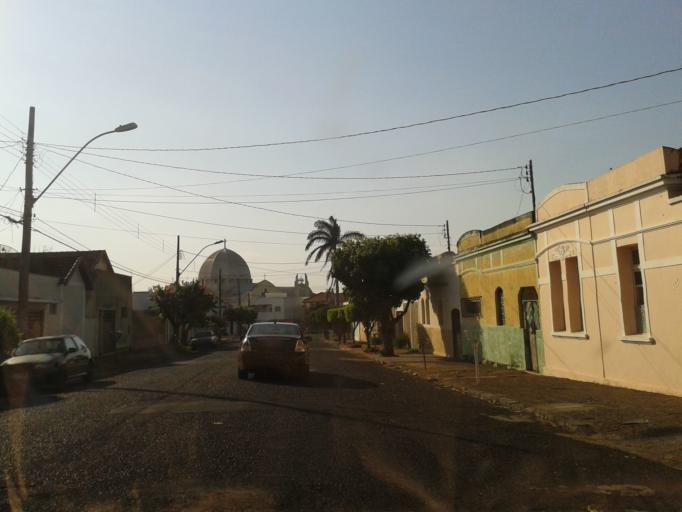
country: BR
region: Minas Gerais
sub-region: Araguari
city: Araguari
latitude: -18.6494
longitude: -48.1864
